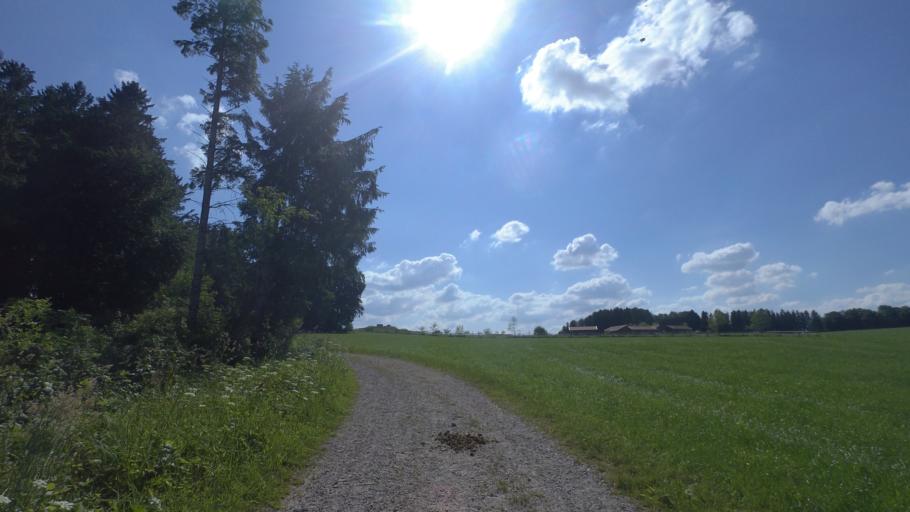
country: DE
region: Bavaria
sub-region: Upper Bavaria
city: Seeon-Seebruck
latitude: 47.9562
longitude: 12.5089
